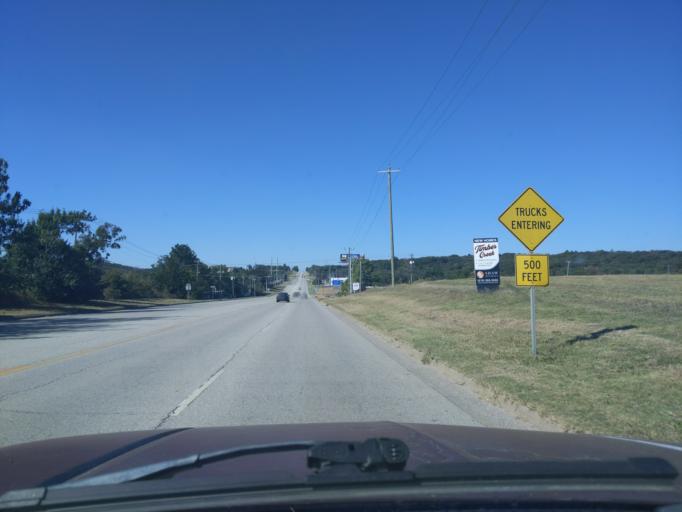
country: US
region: Oklahoma
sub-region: Tulsa County
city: Glenpool
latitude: 35.9885
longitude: -96.0280
